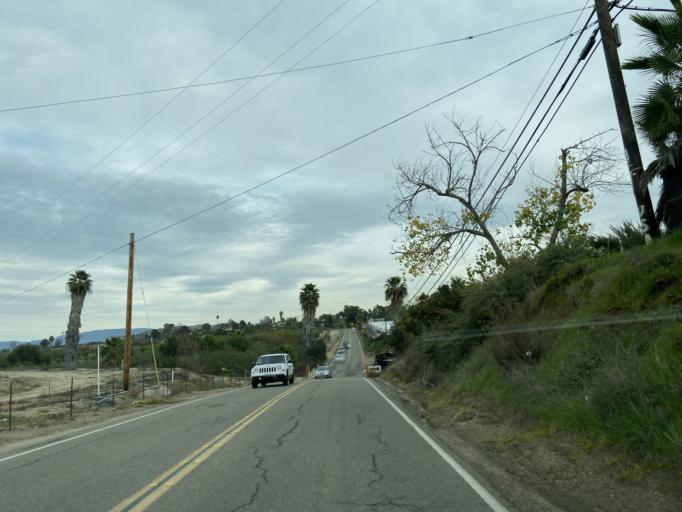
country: US
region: California
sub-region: San Diego County
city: Bonsall
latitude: 33.2635
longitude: -117.2495
